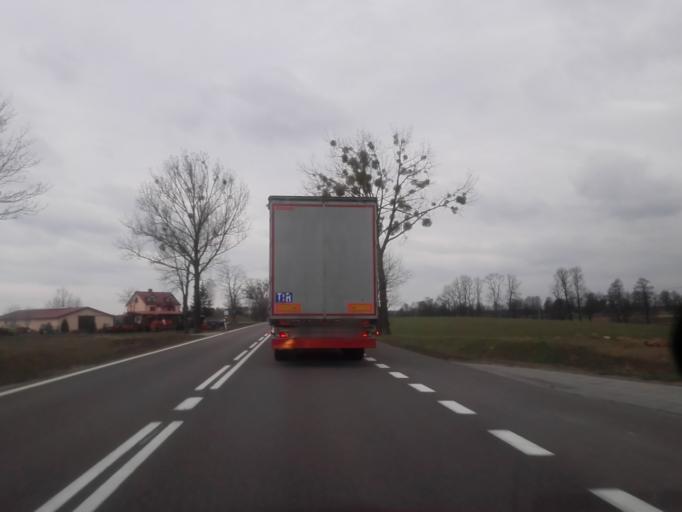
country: PL
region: Podlasie
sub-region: Powiat augustowski
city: Augustow
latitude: 53.7933
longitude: 22.8697
